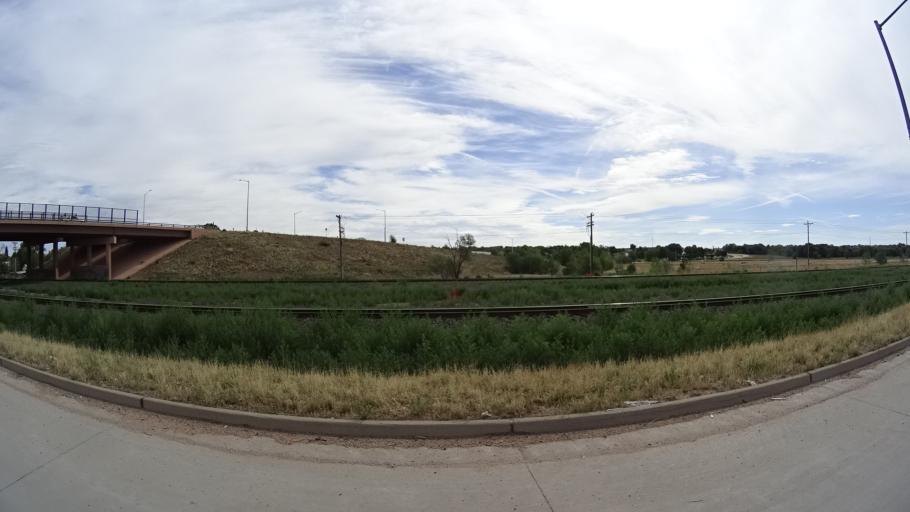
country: US
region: Colorado
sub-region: El Paso County
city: Security-Widefield
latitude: 38.7220
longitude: -104.7180
